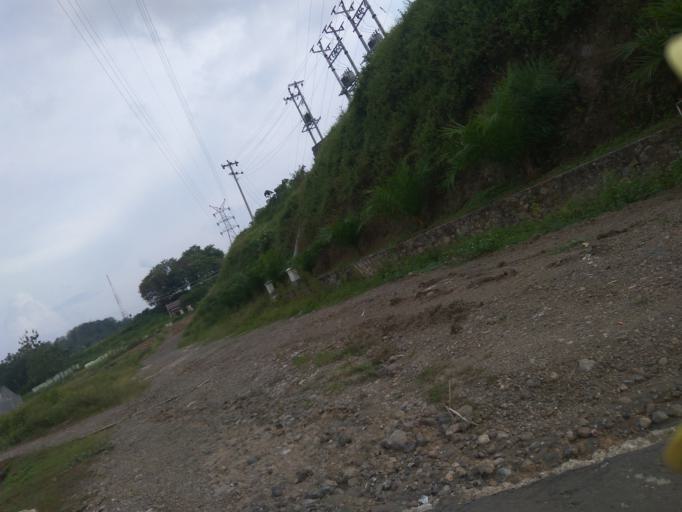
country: ID
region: Central Java
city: Semarang
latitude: -7.0370
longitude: 110.4386
